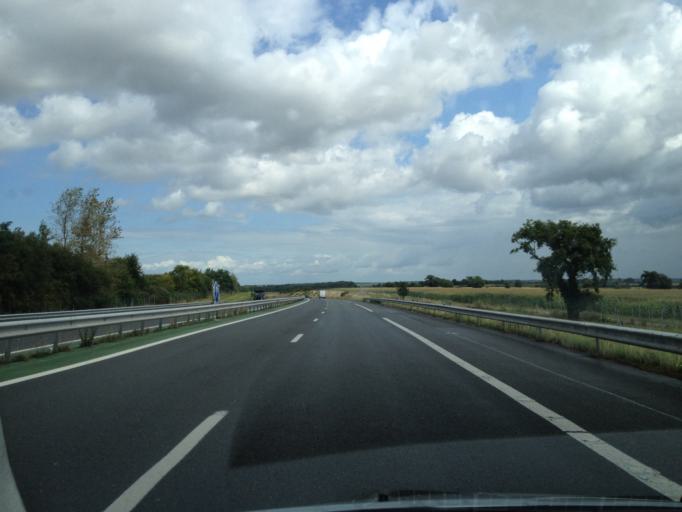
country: FR
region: Pays de la Loire
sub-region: Departement de Maine-et-Loire
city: Saint-Lambert-du-Lattay
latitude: 47.2591
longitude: -0.6170
